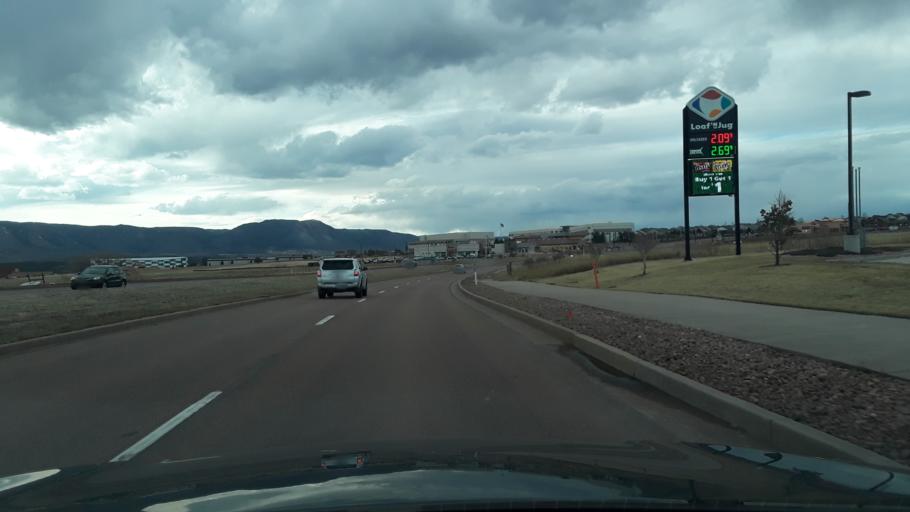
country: US
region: Colorado
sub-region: El Paso County
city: Gleneagle
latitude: 39.0214
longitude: -104.8146
